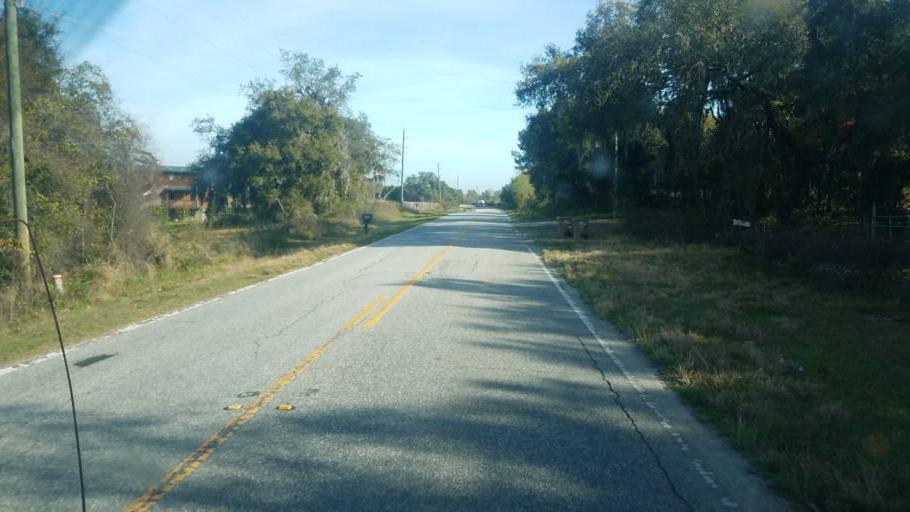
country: US
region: Florida
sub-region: Lake County
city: Clermont
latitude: 28.4479
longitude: -81.7980
